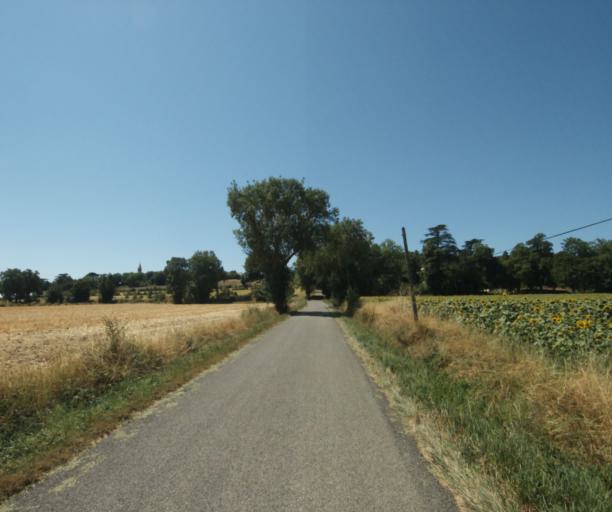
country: FR
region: Midi-Pyrenees
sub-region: Departement de la Haute-Garonne
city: Saint-Felix-Lauragais
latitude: 43.4831
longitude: 1.9259
